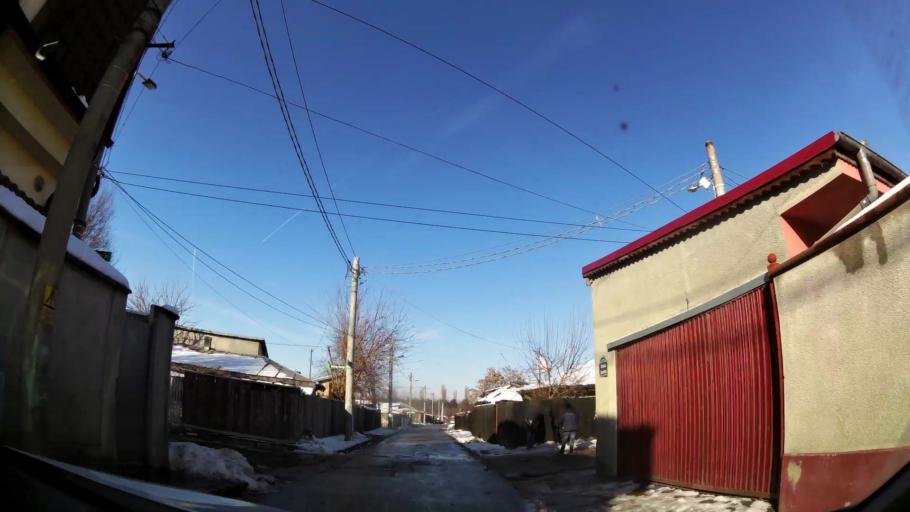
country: RO
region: Ilfov
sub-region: Comuna Fundeni-Dobroesti
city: Fundeni
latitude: 44.4735
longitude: 26.1292
